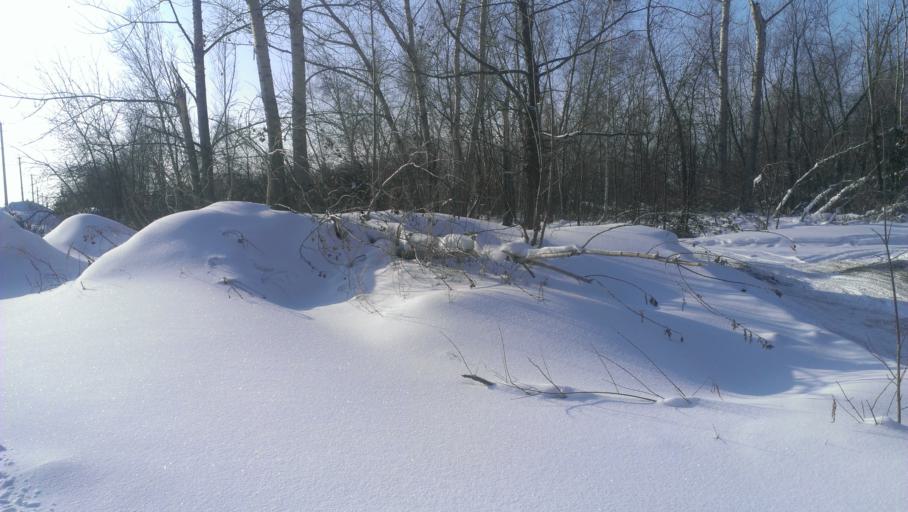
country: RU
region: Altai Krai
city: Zaton
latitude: 53.3181
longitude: 83.8083
